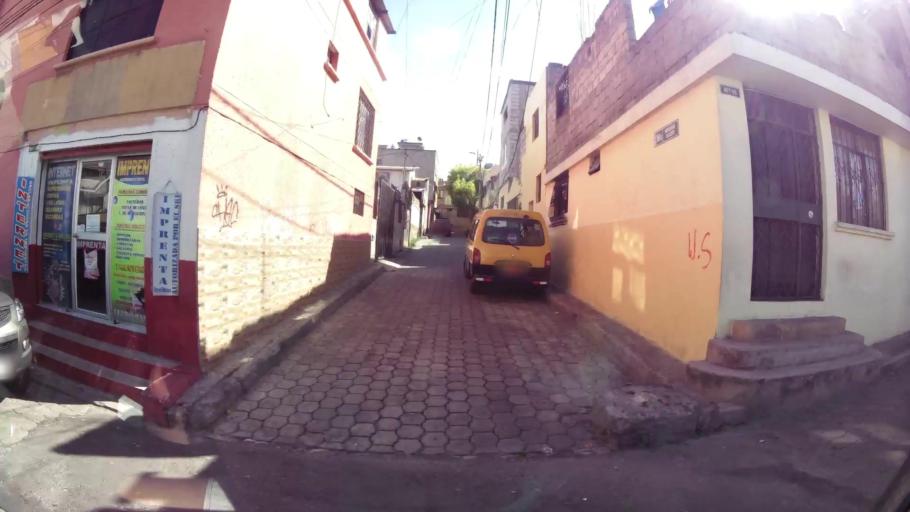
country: EC
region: Pichincha
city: Quito
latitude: -0.1251
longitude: -78.4705
